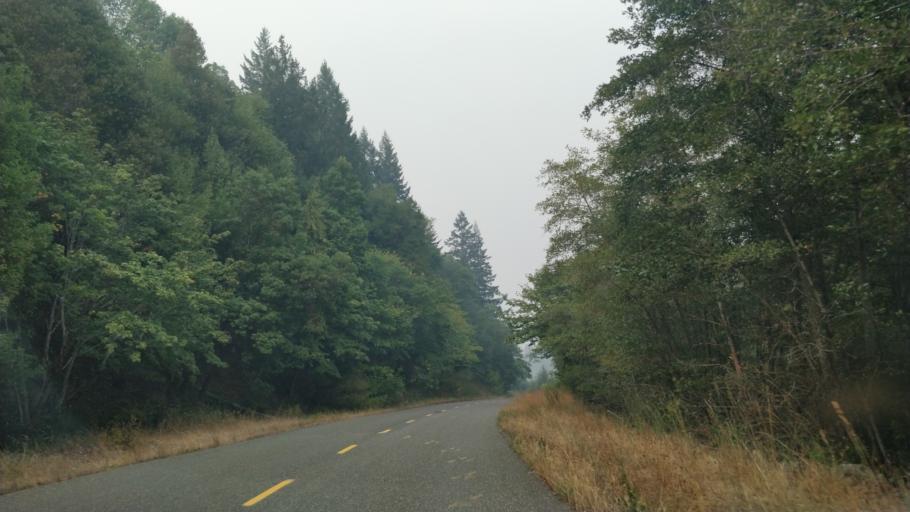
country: US
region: California
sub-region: Humboldt County
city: Rio Dell
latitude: 40.3386
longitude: -124.0273
